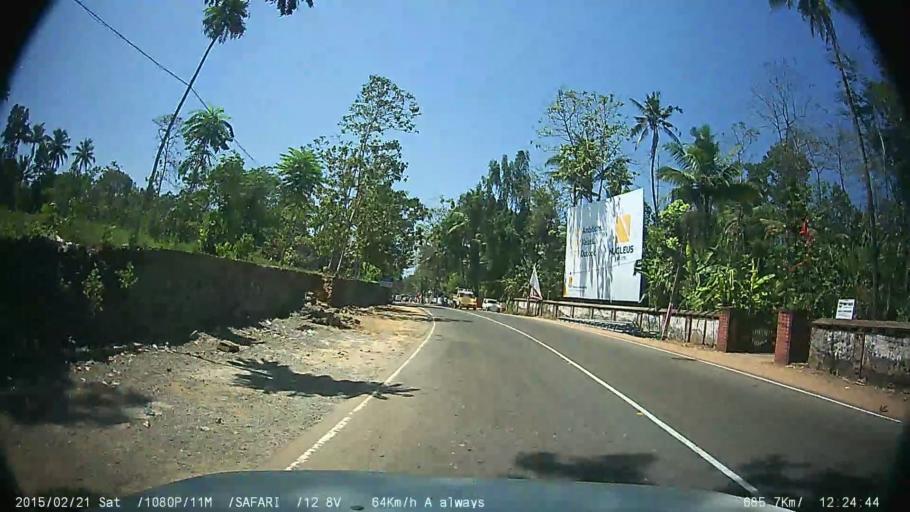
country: IN
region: Kerala
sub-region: Kottayam
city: Palackattumala
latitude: 9.6702
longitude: 76.5801
